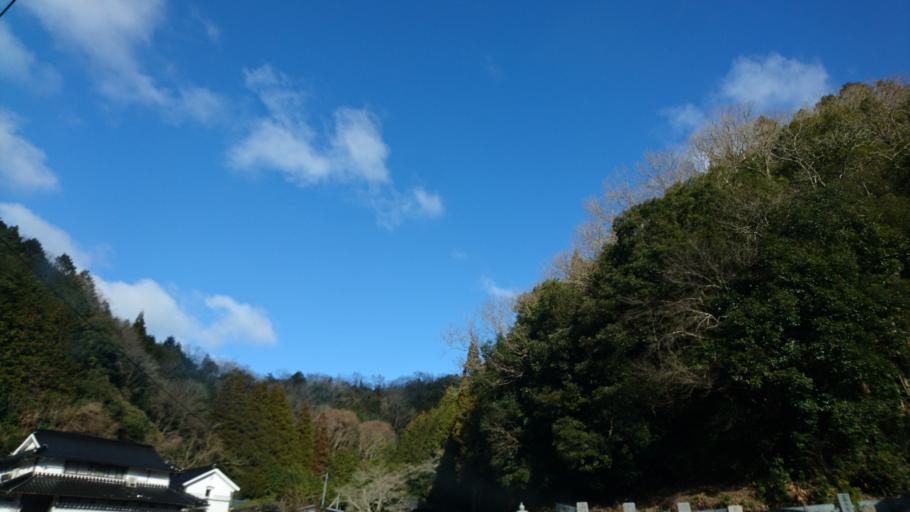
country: JP
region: Okayama
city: Takahashi
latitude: 34.8615
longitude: 133.5664
